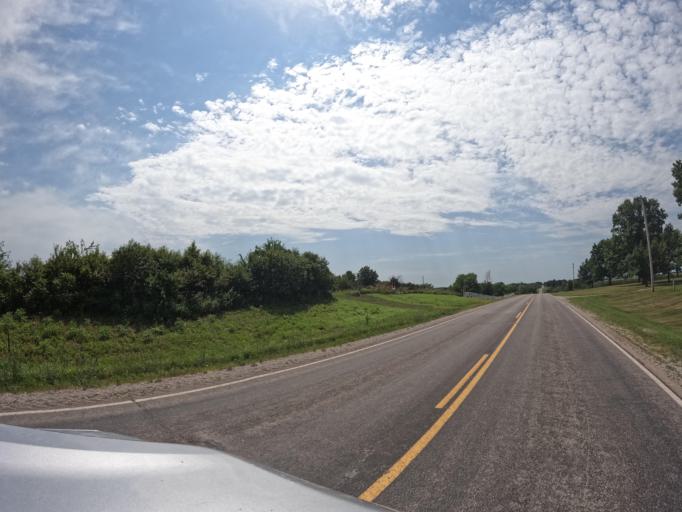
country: US
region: Iowa
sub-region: Appanoose County
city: Centerville
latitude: 40.8029
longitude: -92.9448
